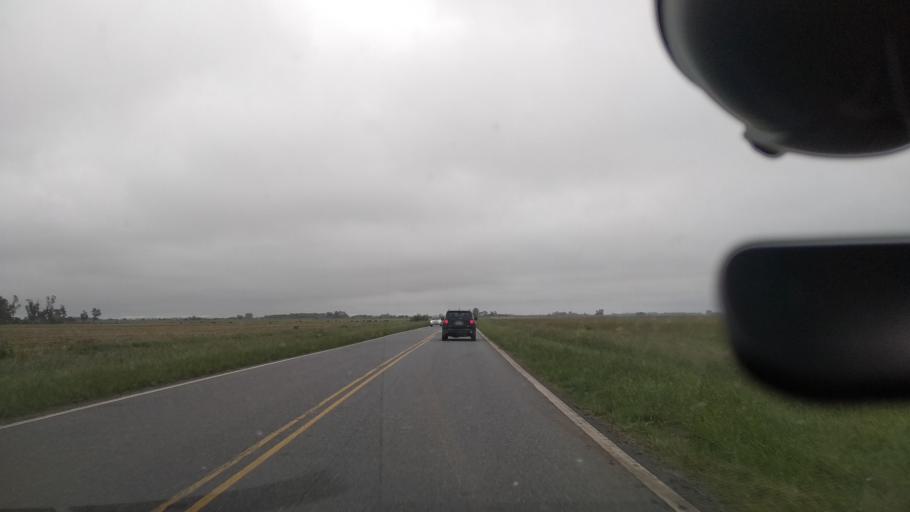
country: AR
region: Buenos Aires
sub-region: Partido de Magdalena
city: Magdalena
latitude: -35.2547
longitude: -57.6643
